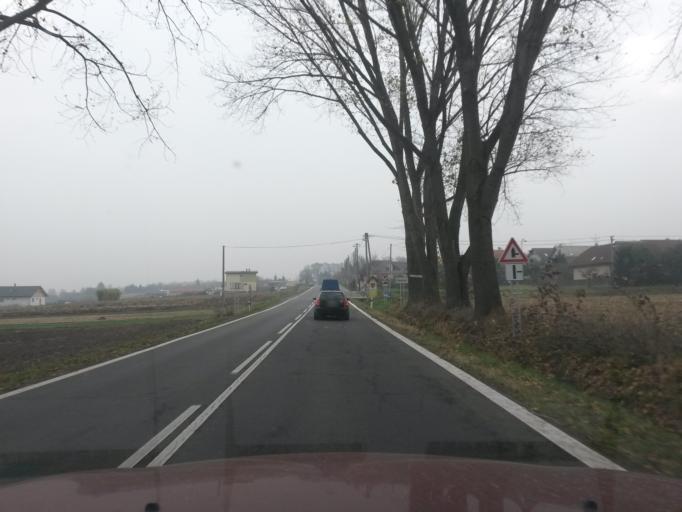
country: SK
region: Kosicky
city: Kosice
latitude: 48.8061
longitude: 21.3017
